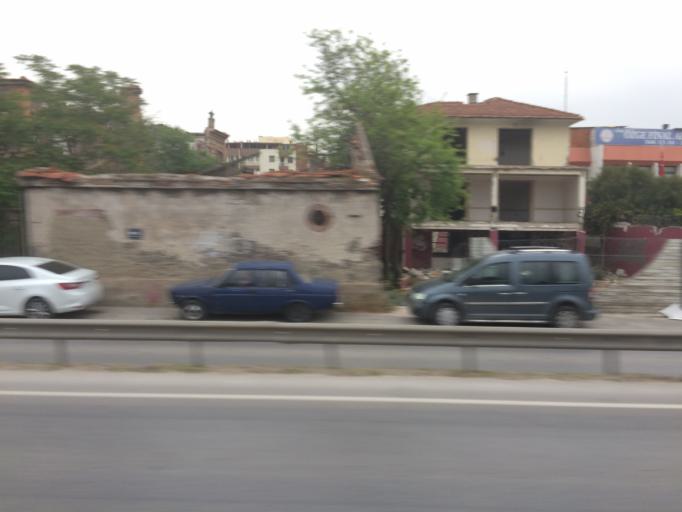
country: TR
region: Izmir
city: Karsiyaka
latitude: 38.4630
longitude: 27.1636
